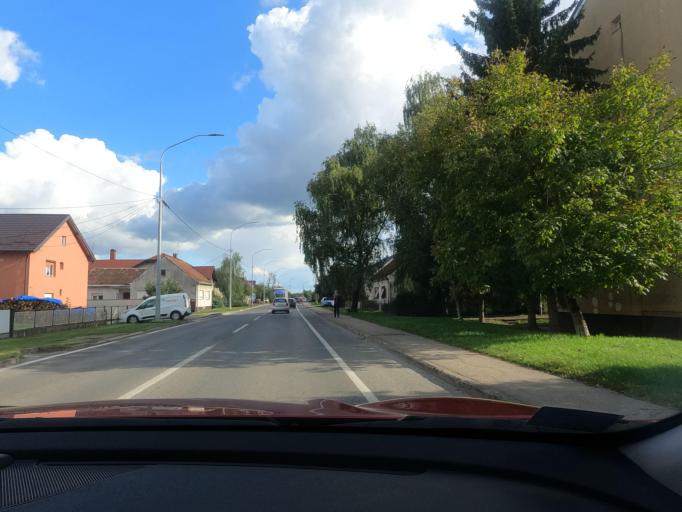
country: HR
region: Sisacko-Moslavacka
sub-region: Grad Sisak
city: Sisak
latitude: 45.4696
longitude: 16.3676
